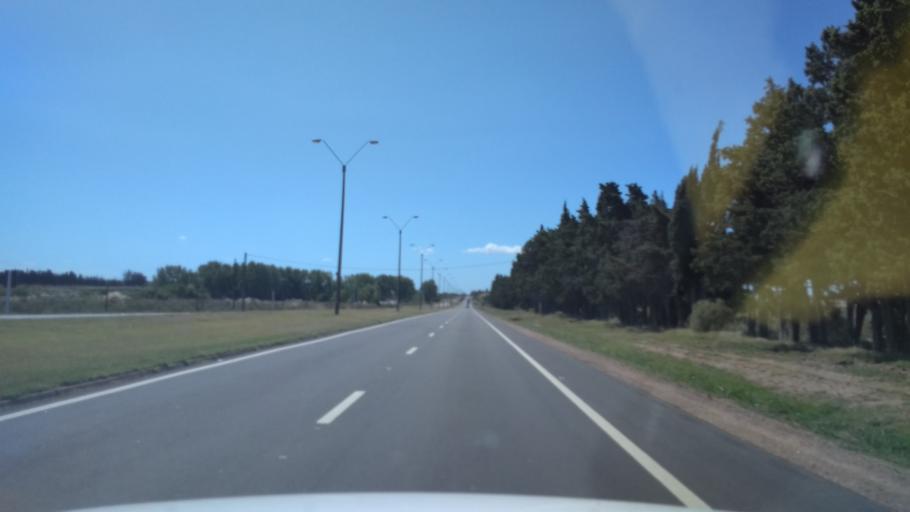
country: UY
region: Canelones
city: Joanico
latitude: -34.5825
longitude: -56.2643
